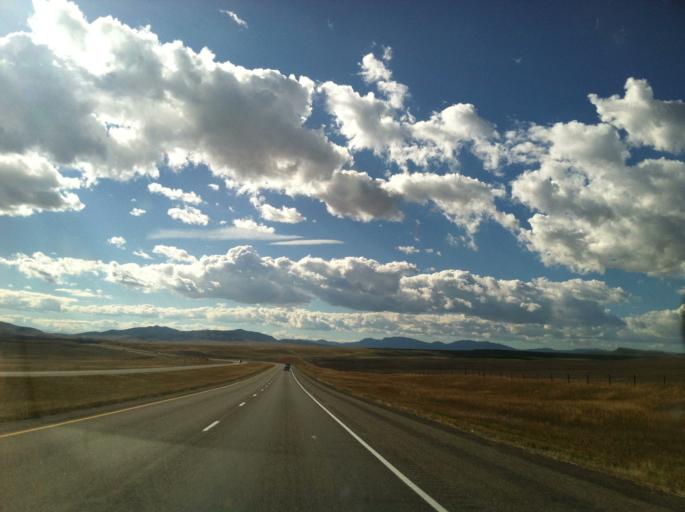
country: US
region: Montana
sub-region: Gallatin County
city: Three Forks
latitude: 45.9202
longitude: -111.6940
